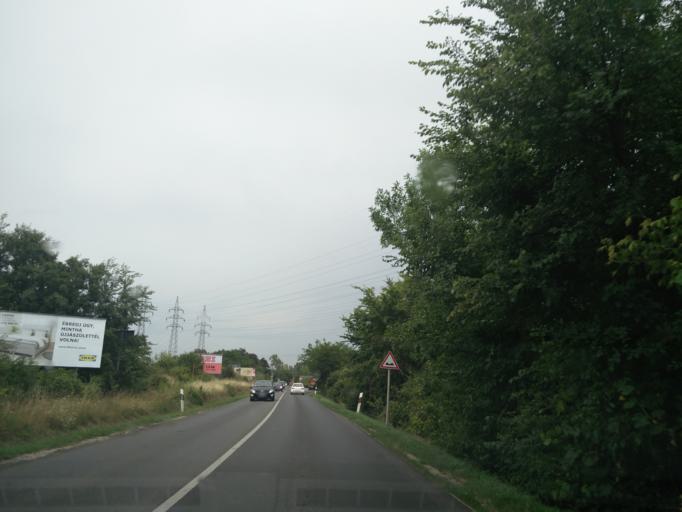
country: HU
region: Pest
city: Toeroekbalint
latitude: 47.4611
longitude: 18.9019
